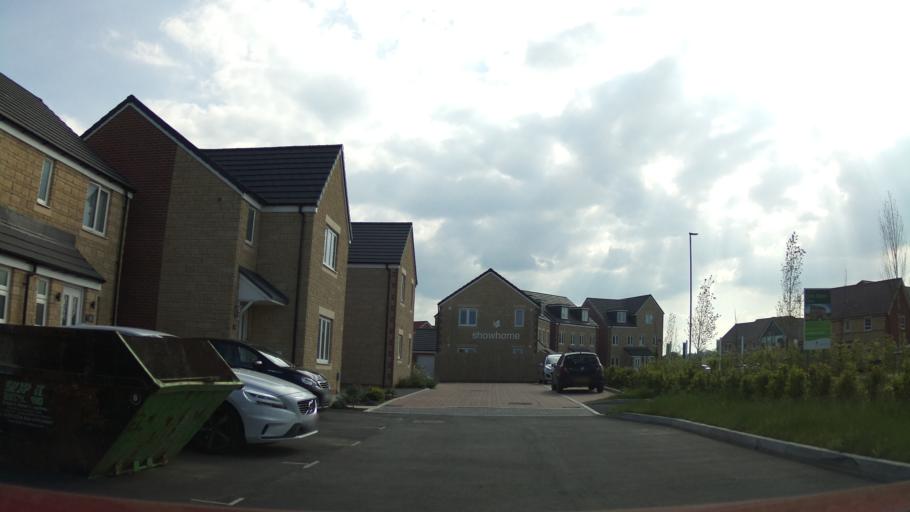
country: GB
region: England
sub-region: Wiltshire
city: Chippenham
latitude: 51.4742
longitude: -2.1128
